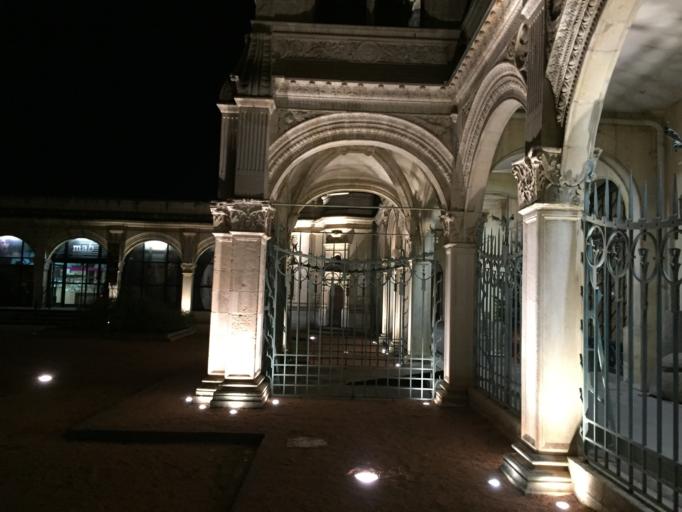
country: FR
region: Auvergne
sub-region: Departement de l'Allier
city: Moulins
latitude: 46.5672
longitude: 3.3304
